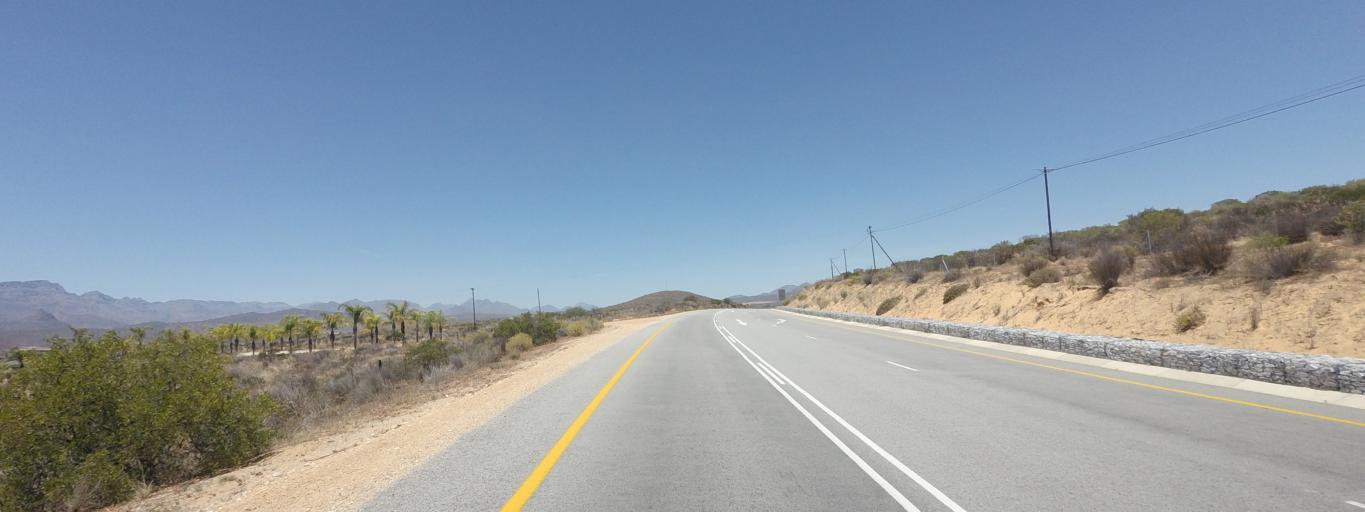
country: ZA
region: Western Cape
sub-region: West Coast District Municipality
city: Clanwilliam
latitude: -32.1624
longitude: 18.8718
